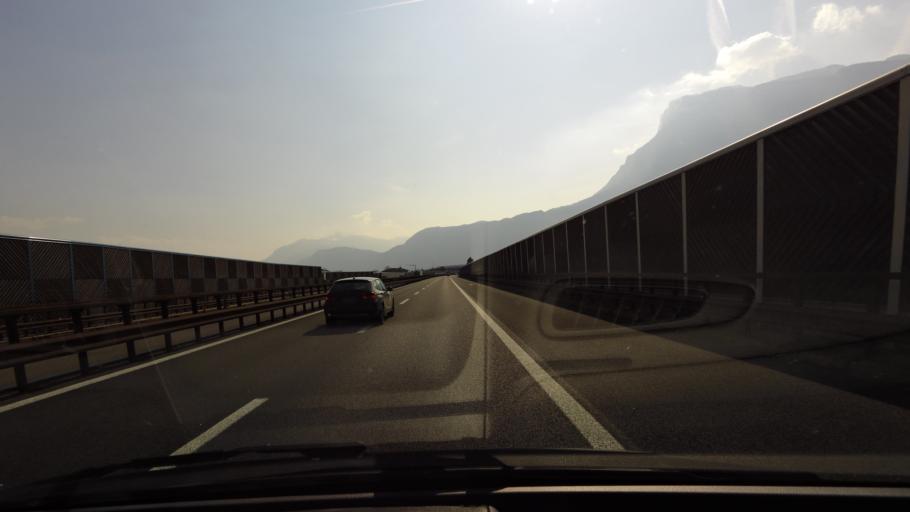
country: IT
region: Trentino-Alto Adige
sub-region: Provincia di Trento
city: Nave San Rocco
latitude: 46.1718
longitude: 11.1061
